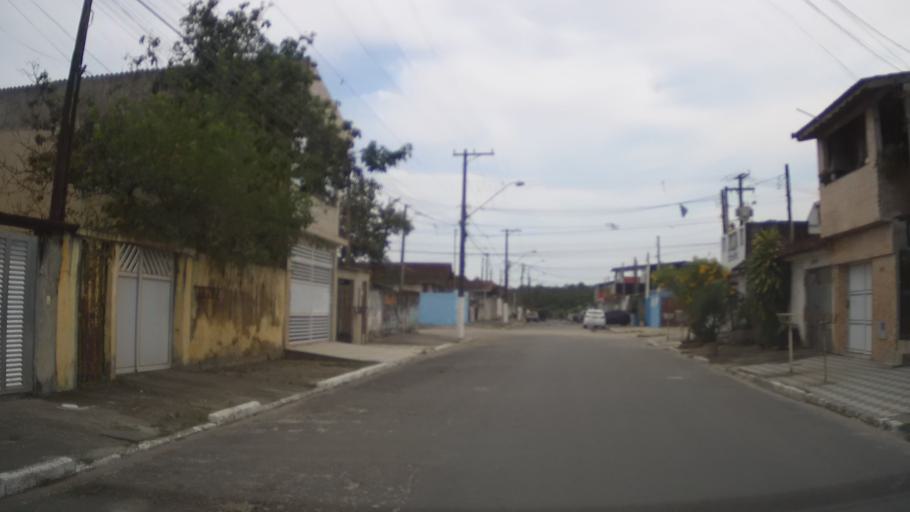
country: BR
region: Sao Paulo
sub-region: Praia Grande
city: Praia Grande
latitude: -24.0062
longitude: -46.4604
